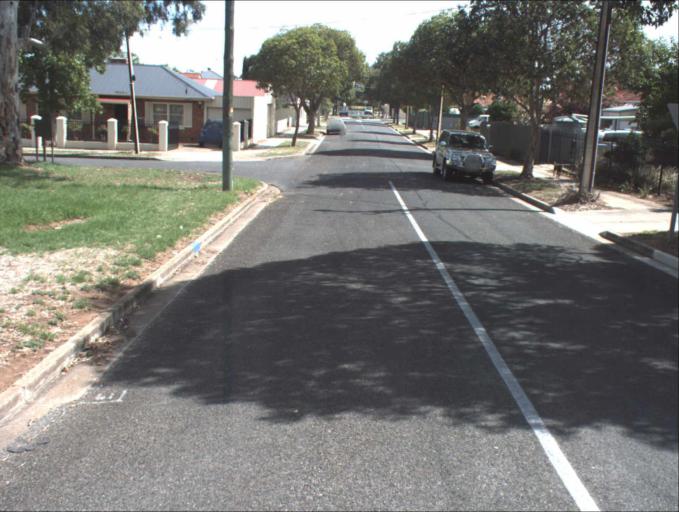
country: AU
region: South Australia
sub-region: Port Adelaide Enfield
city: Blair Athol
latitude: -34.8573
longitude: 138.5984
